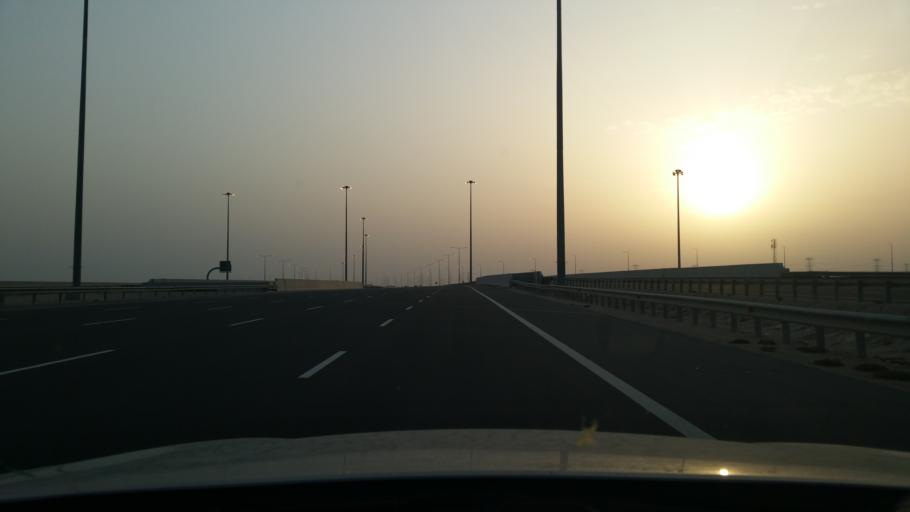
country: QA
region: Baladiyat az Za`ayin
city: Az Za`ayin
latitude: 25.6419
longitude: 51.3973
